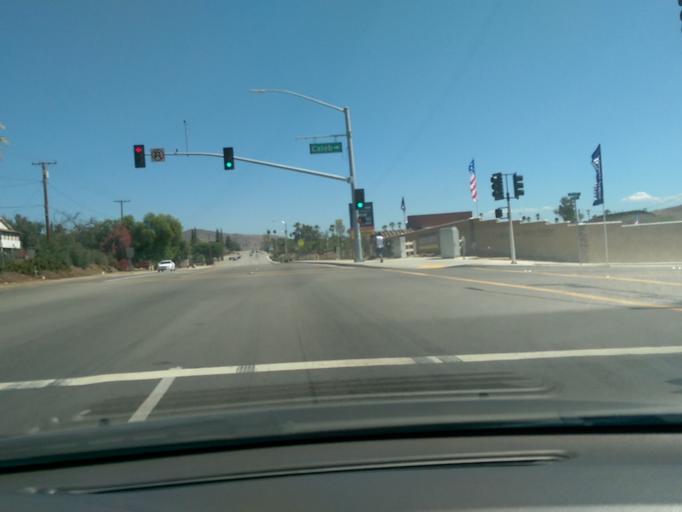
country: US
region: California
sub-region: Riverside County
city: Sunnyslope
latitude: 34.0117
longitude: -117.4539
